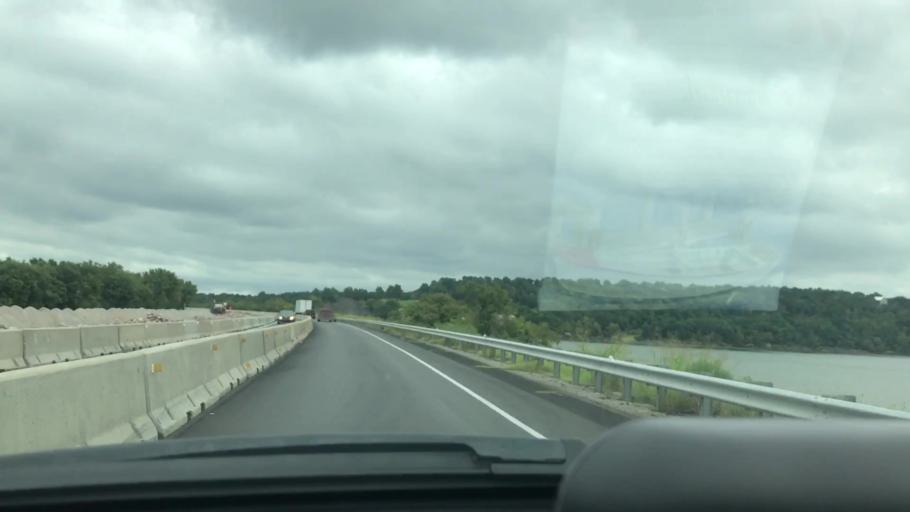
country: US
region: Oklahoma
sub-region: McIntosh County
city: Eufaula
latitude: 35.2431
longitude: -95.5861
